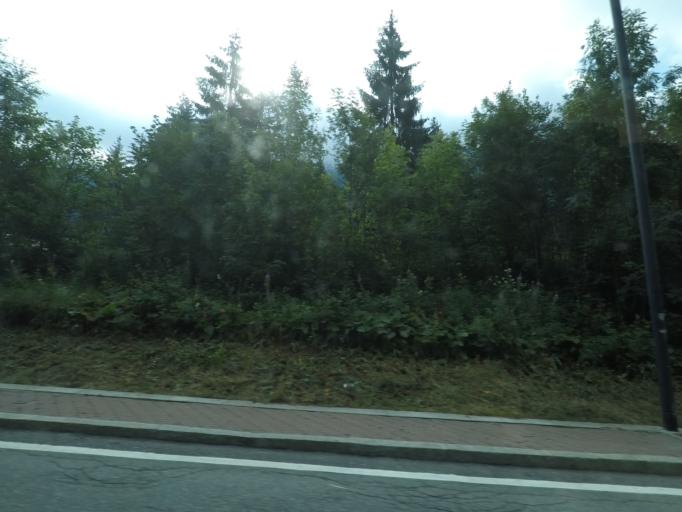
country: IT
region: Aosta Valley
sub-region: Valle d'Aosta
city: Valtournenche
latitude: 45.8676
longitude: 7.6121
